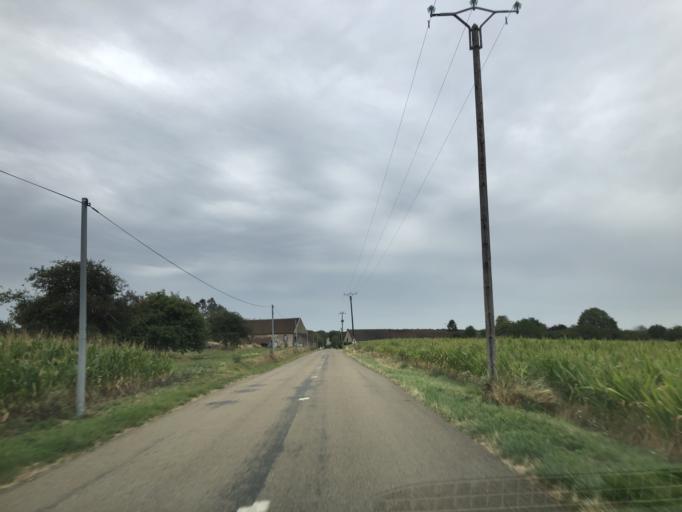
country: FR
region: Centre
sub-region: Departement du Loiret
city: Douchy
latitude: 47.9758
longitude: 3.1428
